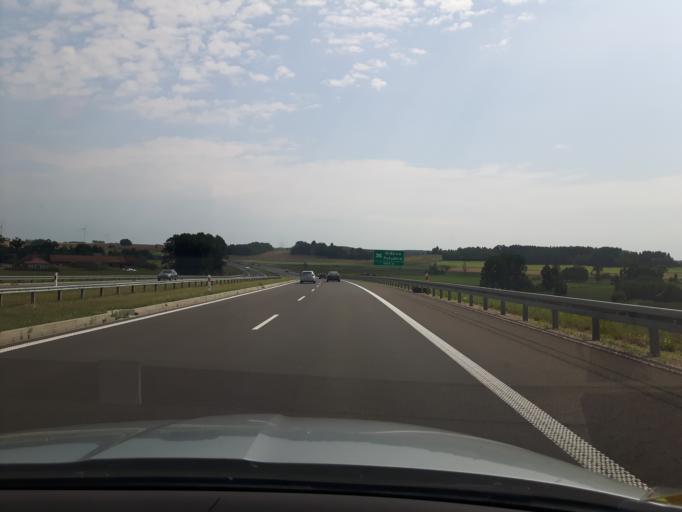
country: PL
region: Warmian-Masurian Voivodeship
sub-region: Powiat nidzicki
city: Nidzica
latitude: 53.3453
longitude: 20.3967
